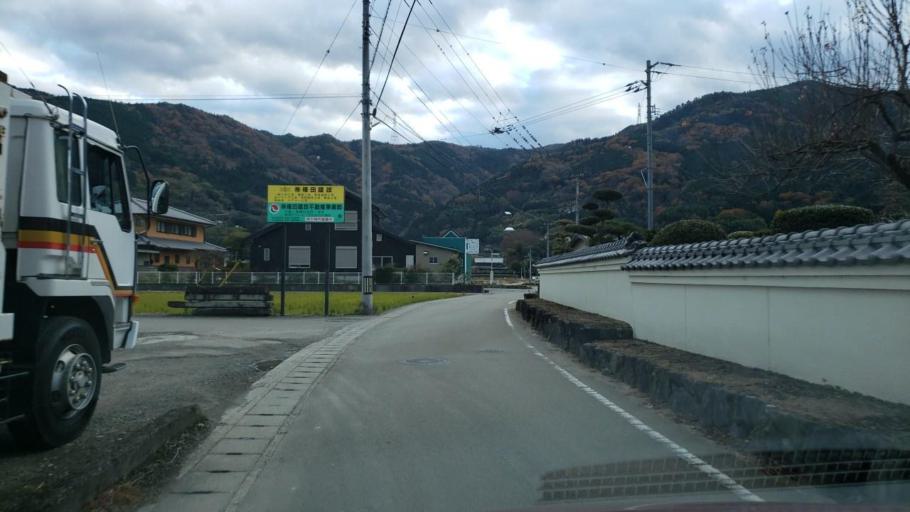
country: JP
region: Tokushima
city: Wakimachi
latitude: 34.0599
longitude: 134.1434
